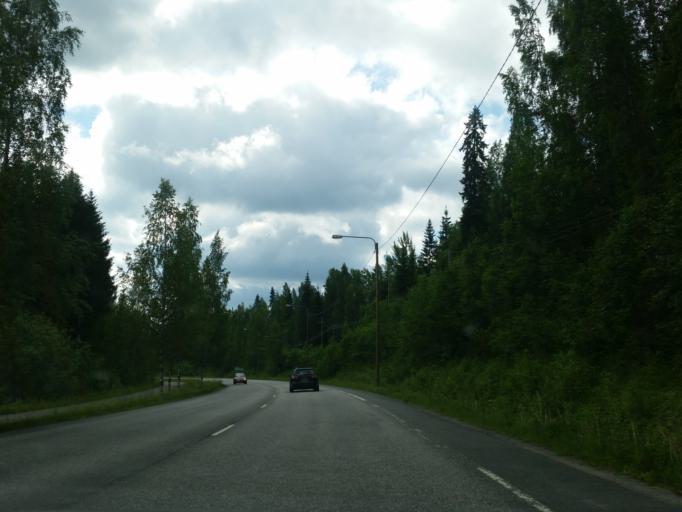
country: FI
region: Northern Savo
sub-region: Kuopio
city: Kuopio
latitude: 62.8413
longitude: 27.5560
